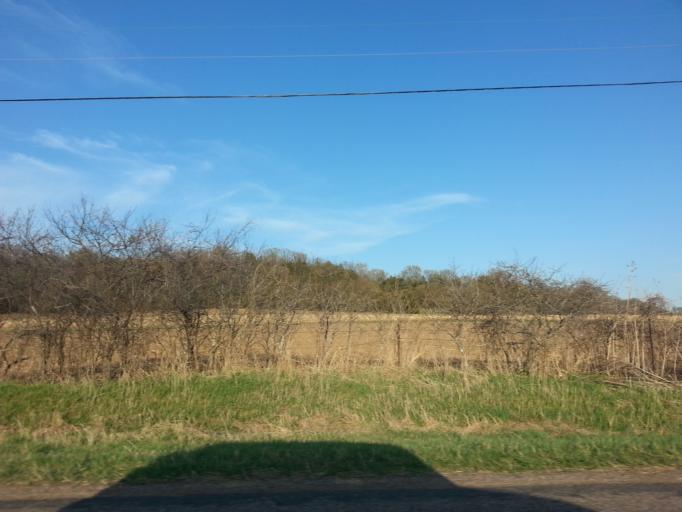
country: US
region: Wisconsin
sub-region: Pierce County
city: River Falls
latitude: 44.8785
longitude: -92.6496
